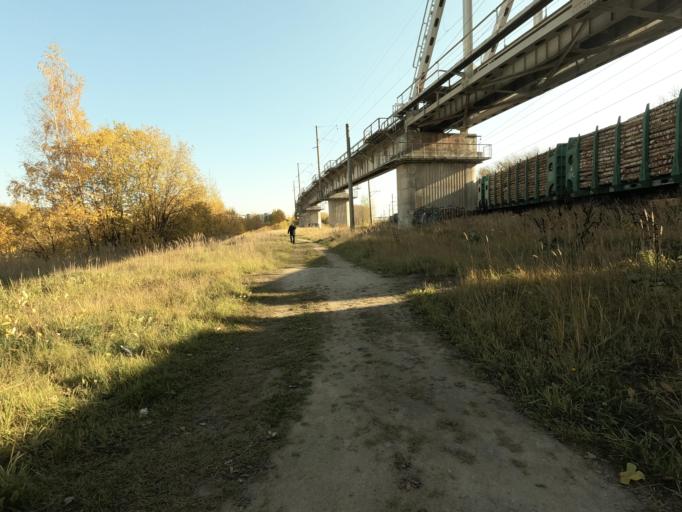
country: RU
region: Leningrad
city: Rybatskoye
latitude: 59.8406
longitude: 30.4772
